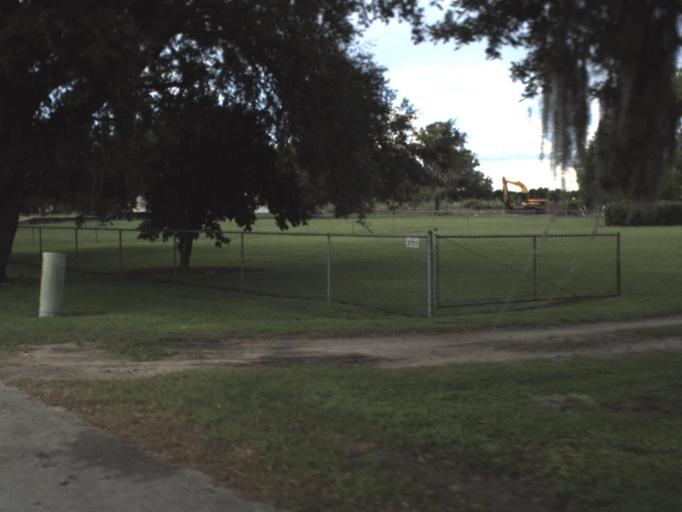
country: US
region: Florida
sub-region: Polk County
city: Fort Meade
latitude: 27.7481
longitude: -81.7585
